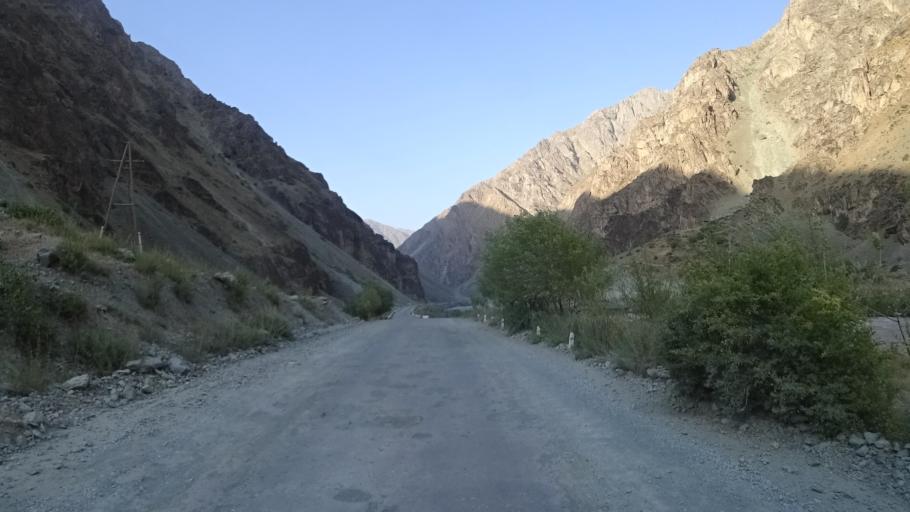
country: TJ
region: Gorno-Badakhshan
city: Qalaikhumb
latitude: 38.4193
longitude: 70.7390
